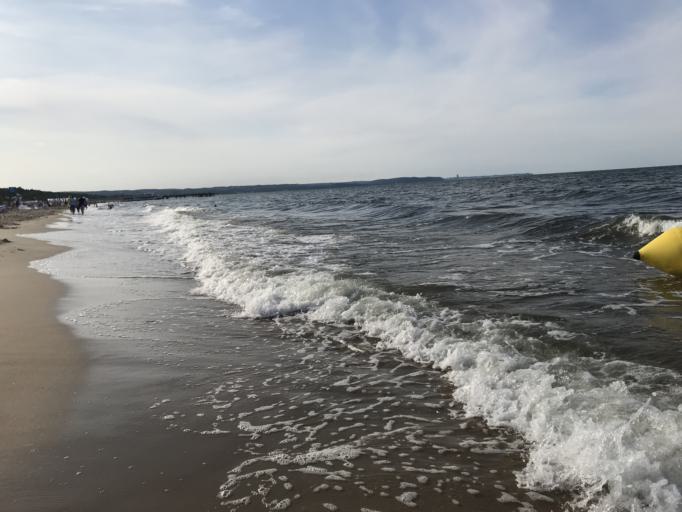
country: PL
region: Pomeranian Voivodeship
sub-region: Gdansk
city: Gdansk
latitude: 54.4113
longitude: 18.6322
